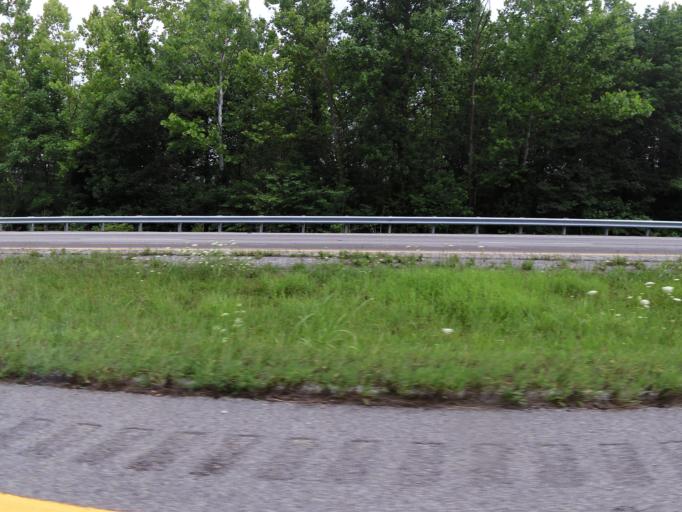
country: US
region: Kentucky
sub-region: Muhlenberg County
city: Central City
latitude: 37.3203
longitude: -87.0220
